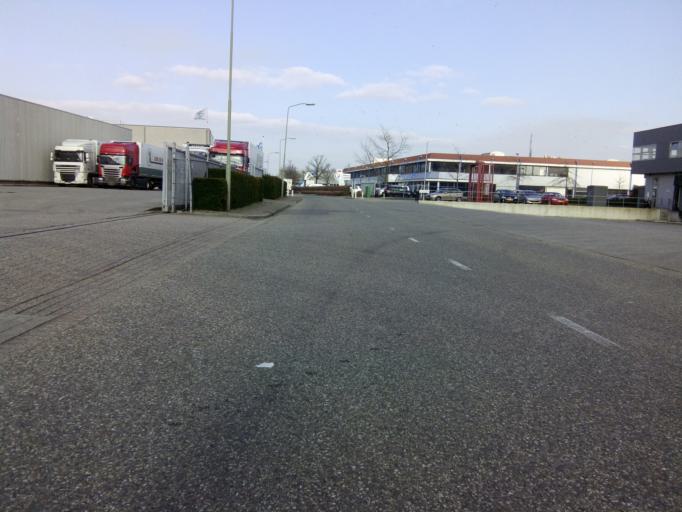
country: NL
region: Utrecht
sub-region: Gemeente Utrechtse Heuvelrug
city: Overberg
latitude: 52.0842
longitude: 5.4694
